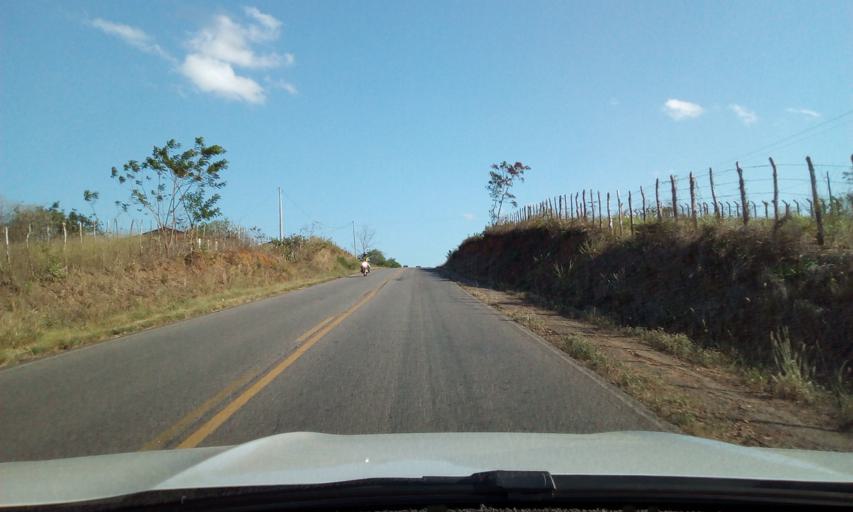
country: BR
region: Paraiba
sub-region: Guarabira
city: Guarabira
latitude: -6.9125
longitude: -35.4520
